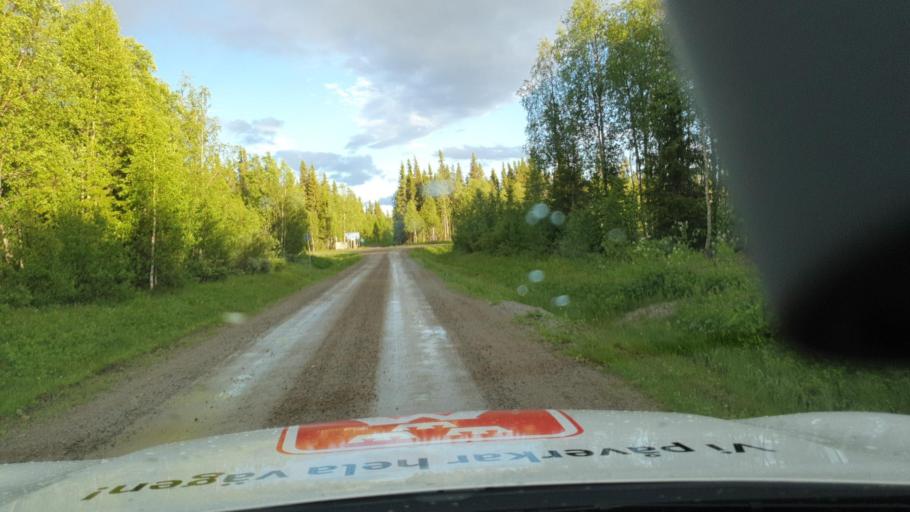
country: SE
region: Vaesterbotten
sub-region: Storumans Kommun
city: Storuman
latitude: 64.7515
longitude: 17.0858
